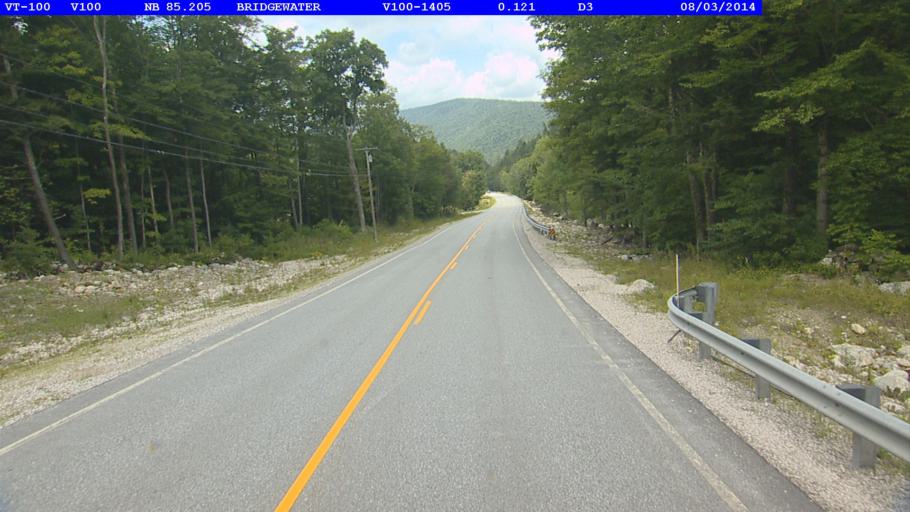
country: US
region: Vermont
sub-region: Rutland County
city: Rutland
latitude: 43.5886
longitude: -72.7553
